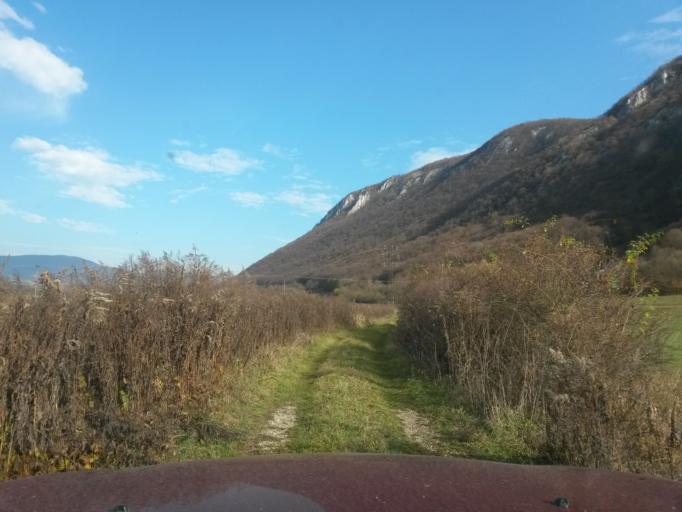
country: SK
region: Kosicky
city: Roznava
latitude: 48.5904
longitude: 20.4811
